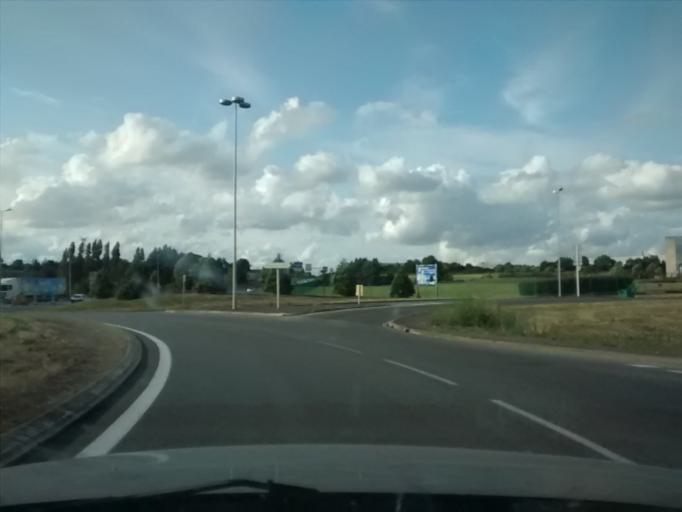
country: FR
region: Pays de la Loire
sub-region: Departement de la Mayenne
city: Laval
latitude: 48.0916
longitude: -0.7507
